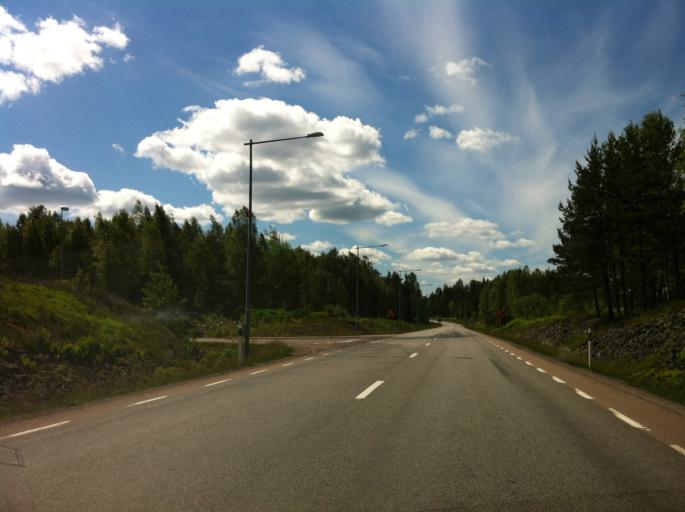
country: SE
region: Vaestra Goetaland
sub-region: Amals Kommun
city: Amal
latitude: 59.0404
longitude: 12.6750
